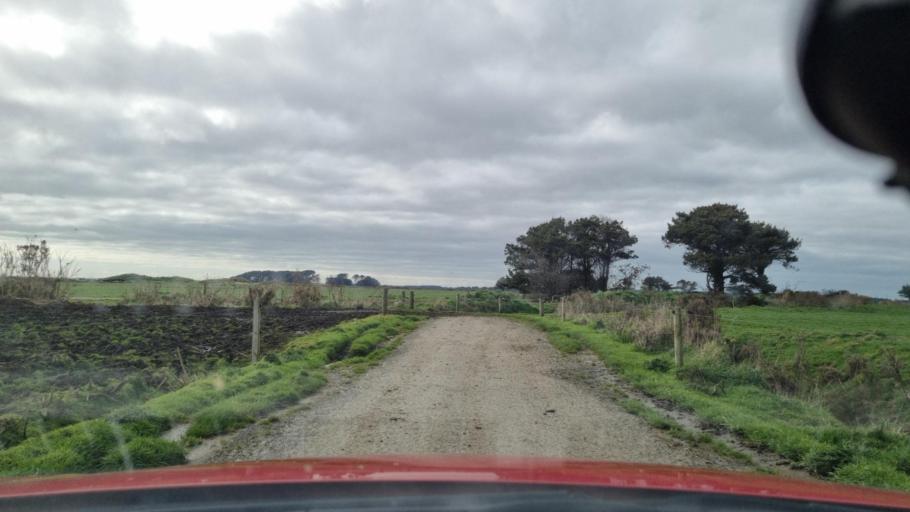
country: NZ
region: Southland
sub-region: Invercargill City
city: Bluff
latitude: -46.5151
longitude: 168.3071
